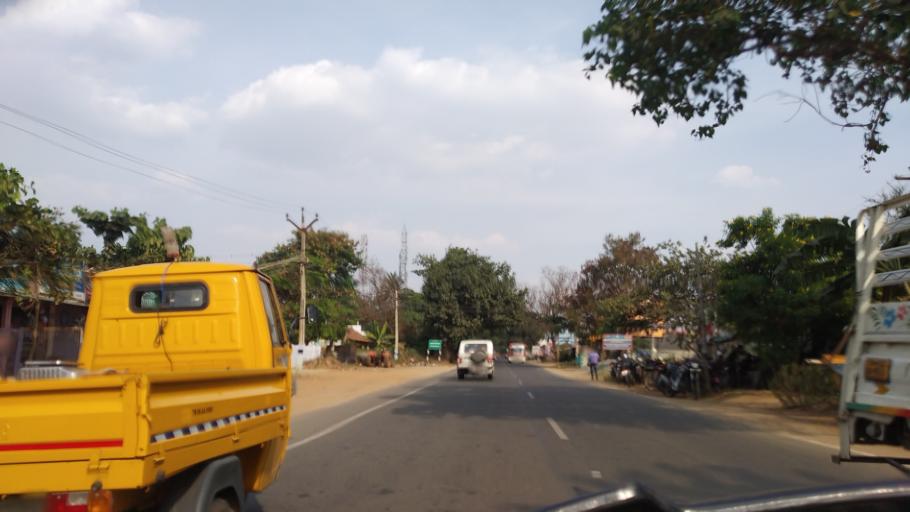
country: IN
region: Tamil Nadu
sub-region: Coimbatore
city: Perur
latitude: 10.9710
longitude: 76.8858
